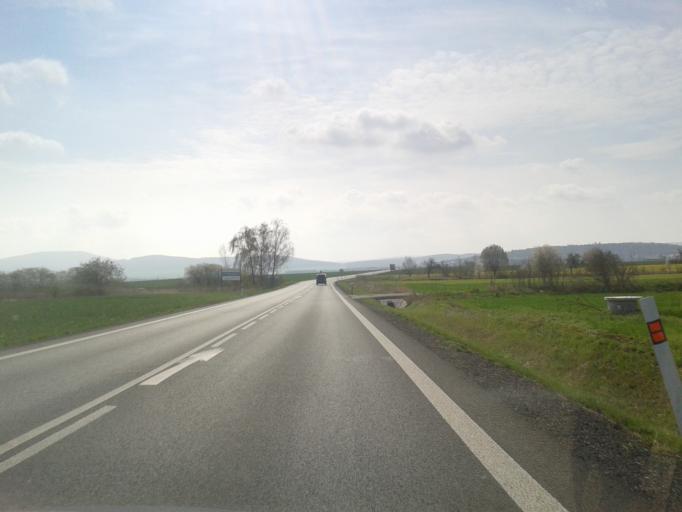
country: CZ
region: Central Bohemia
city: Zebrak
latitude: 49.8569
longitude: 13.9053
